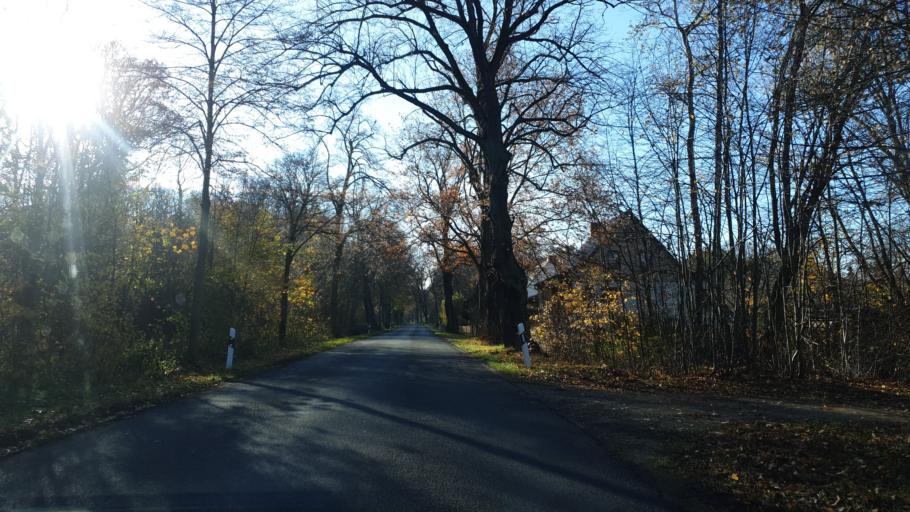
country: DE
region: Saxony-Anhalt
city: Droyssig
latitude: 51.0373
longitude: 12.0264
